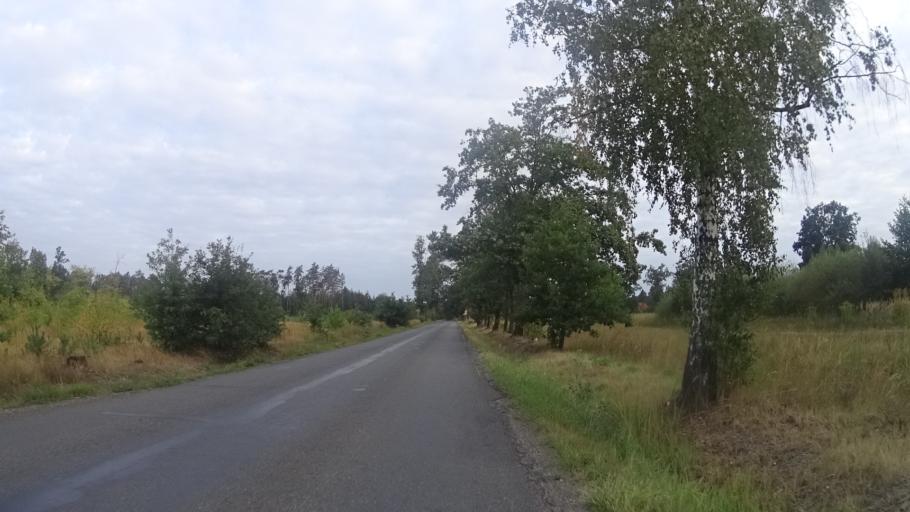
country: CZ
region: Kralovehradecky
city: Cernilov
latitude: 50.2027
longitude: 15.9299
